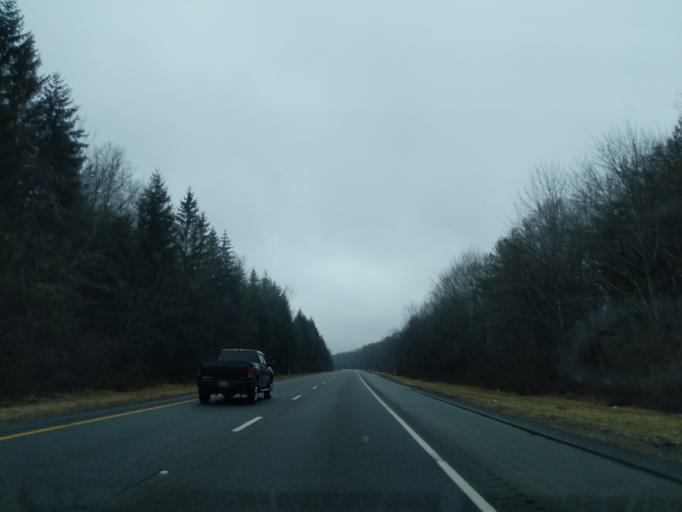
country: US
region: Massachusetts
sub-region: Worcester County
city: Oxford
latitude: 42.0980
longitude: -71.8605
